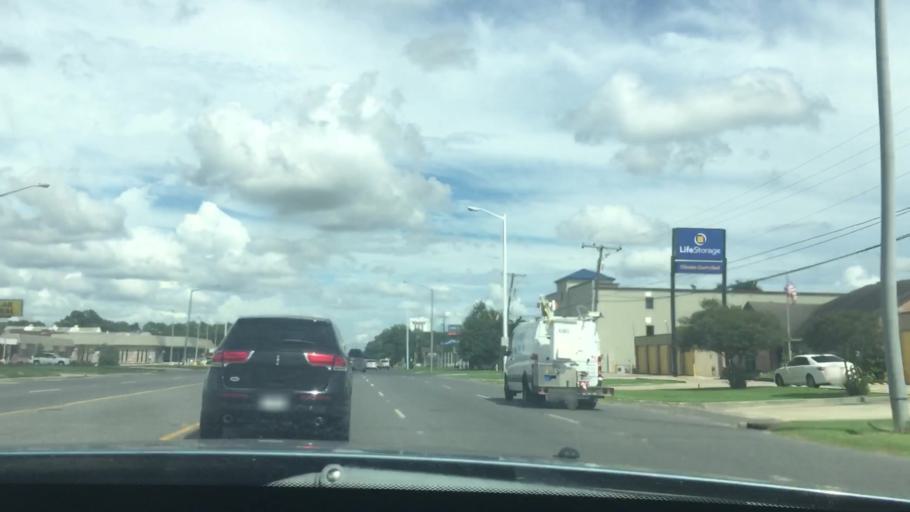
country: US
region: Louisiana
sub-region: East Baton Rouge Parish
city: Baton Rouge
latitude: 30.4507
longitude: -91.1431
